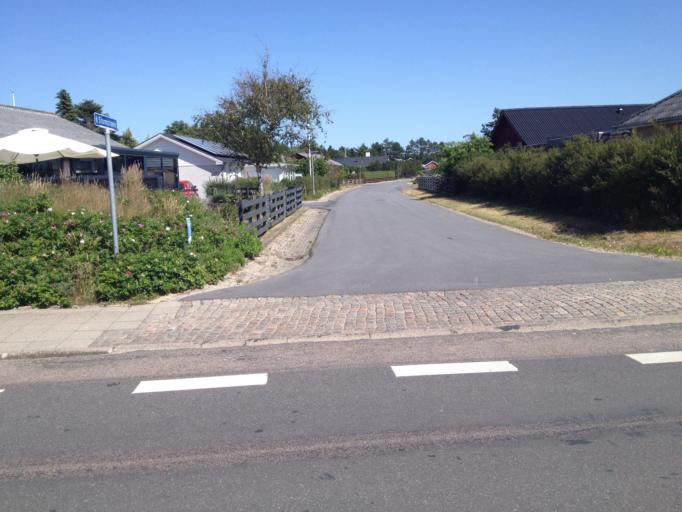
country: DE
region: Schleswig-Holstein
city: List
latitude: 55.0890
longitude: 8.5513
